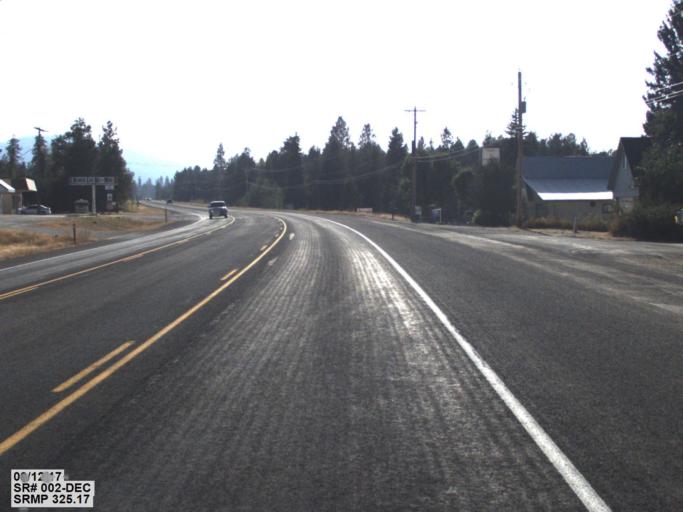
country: US
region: Washington
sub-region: Pend Oreille County
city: Newport
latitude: 48.1198
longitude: -117.2067
